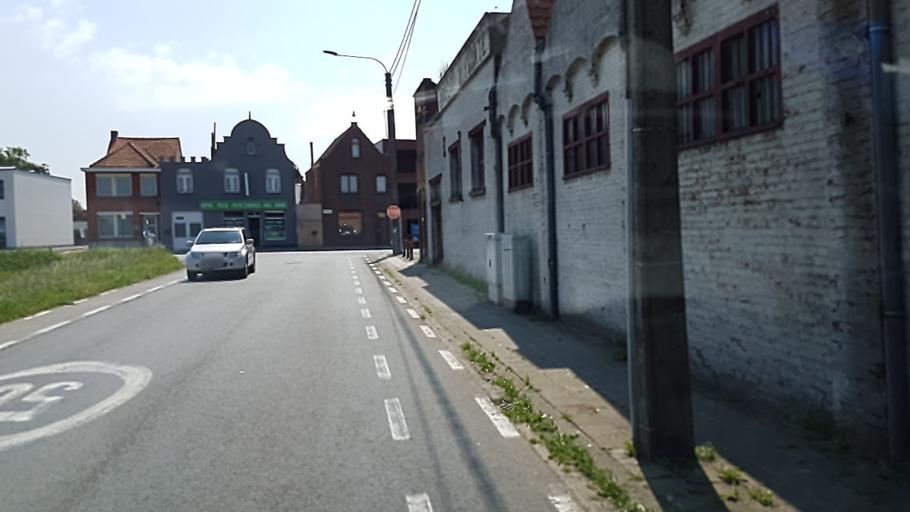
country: BE
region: Flanders
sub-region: Provincie West-Vlaanderen
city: Waregem
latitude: 50.8394
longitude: 3.4071
